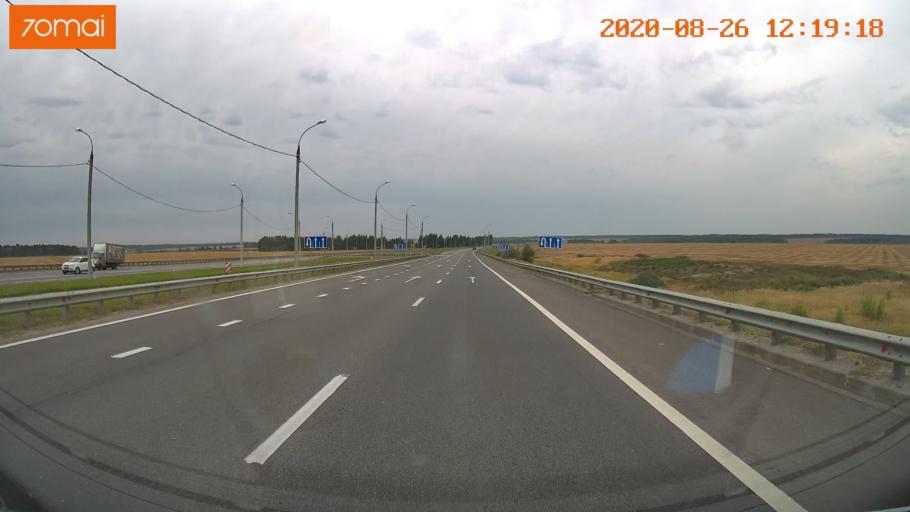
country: RU
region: Rjazan
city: Murmino
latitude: 54.4744
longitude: 40.0009
